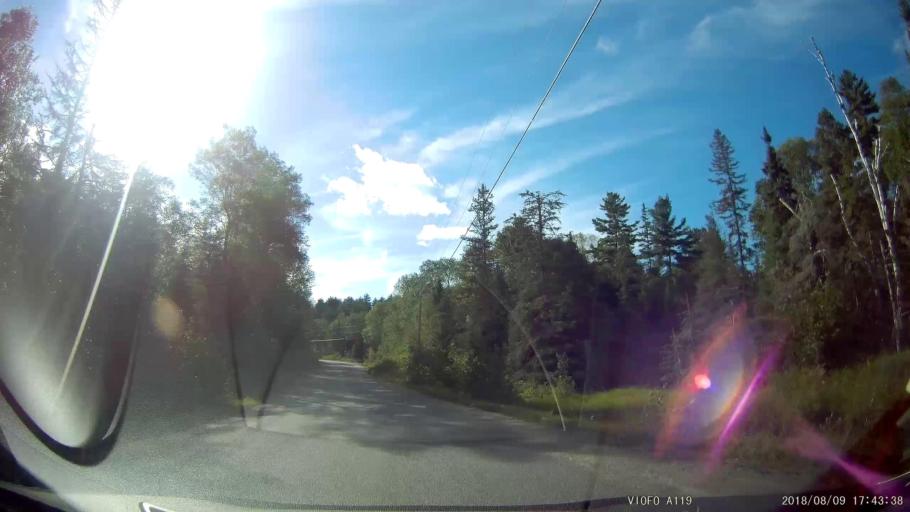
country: CA
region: Ontario
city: Rayside-Balfour
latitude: 46.6089
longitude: -81.5292
